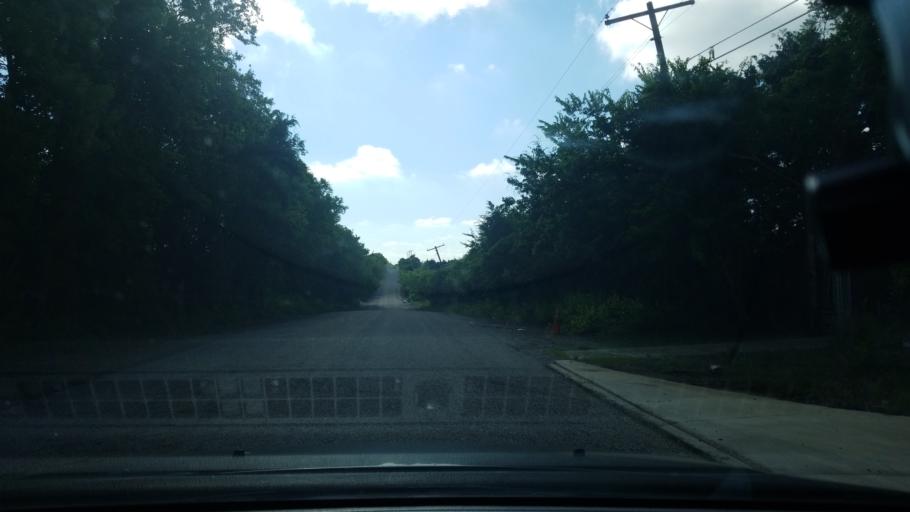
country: US
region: Texas
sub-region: Dallas County
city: Sunnyvale
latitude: 32.8043
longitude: -96.5595
